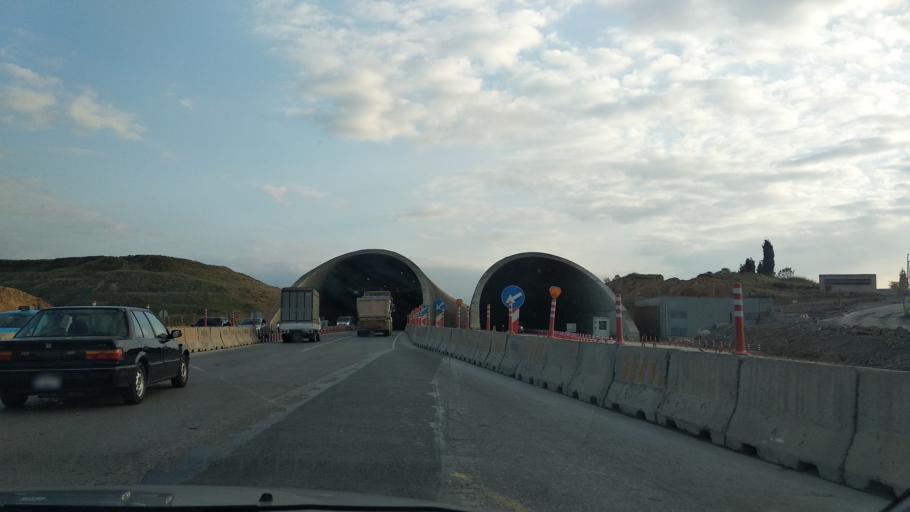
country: TR
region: Istanbul
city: Icmeler
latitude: 40.9044
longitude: 29.3278
